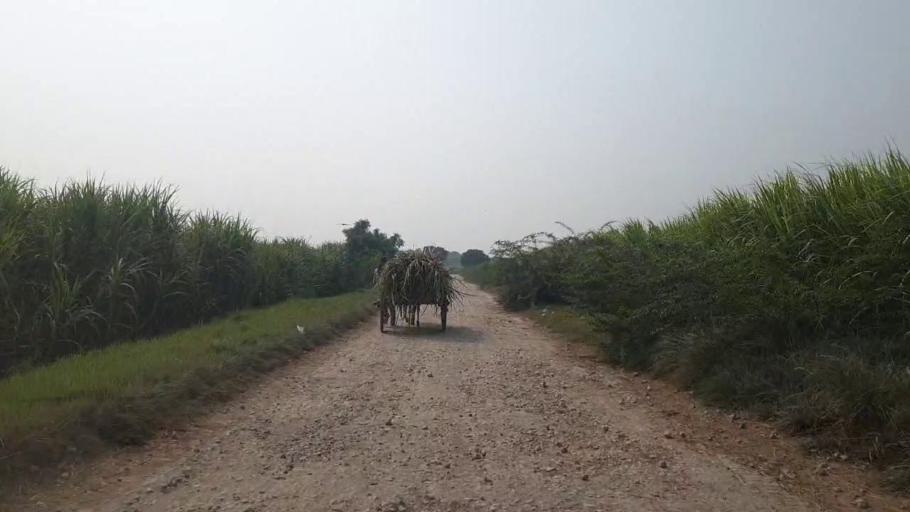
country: PK
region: Sindh
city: Tando Muhammad Khan
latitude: 25.2281
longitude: 68.5657
